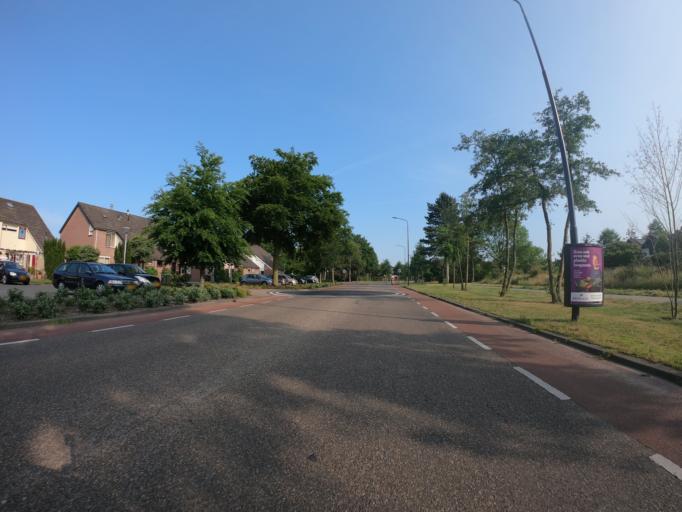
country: NL
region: North Brabant
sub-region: Gemeente Uden
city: Uden
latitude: 51.6686
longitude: 5.6365
